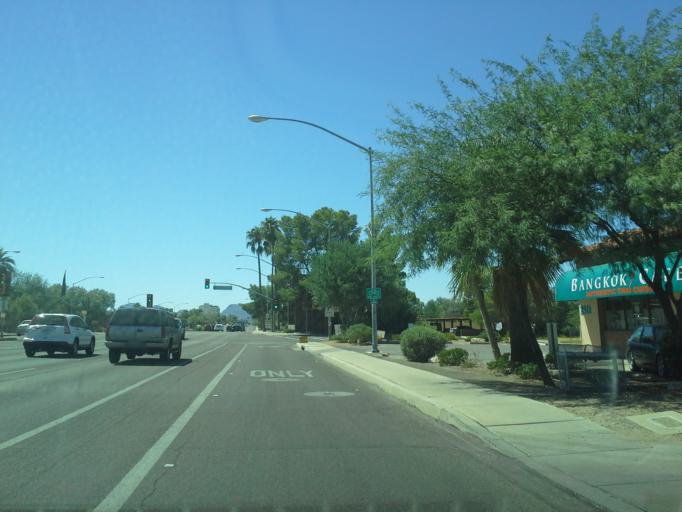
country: US
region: Arizona
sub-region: Pima County
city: Tucson
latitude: 32.2362
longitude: -110.9346
